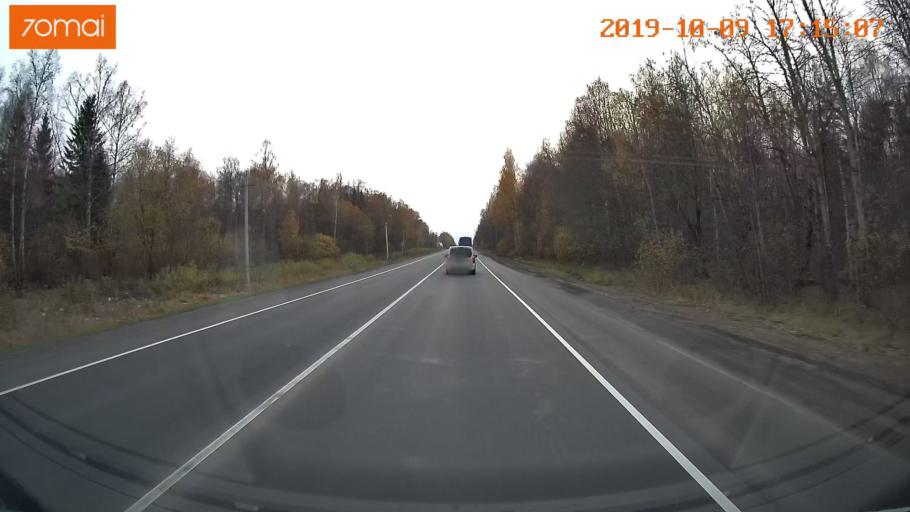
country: RU
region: Ivanovo
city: Furmanov
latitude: 57.2999
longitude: 41.1963
